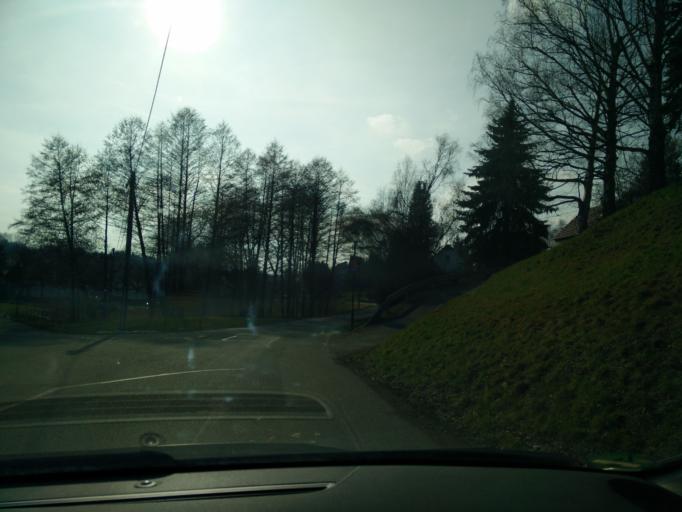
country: DE
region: Saxony
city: Geringswalde
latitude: 51.1128
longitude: 12.8741
